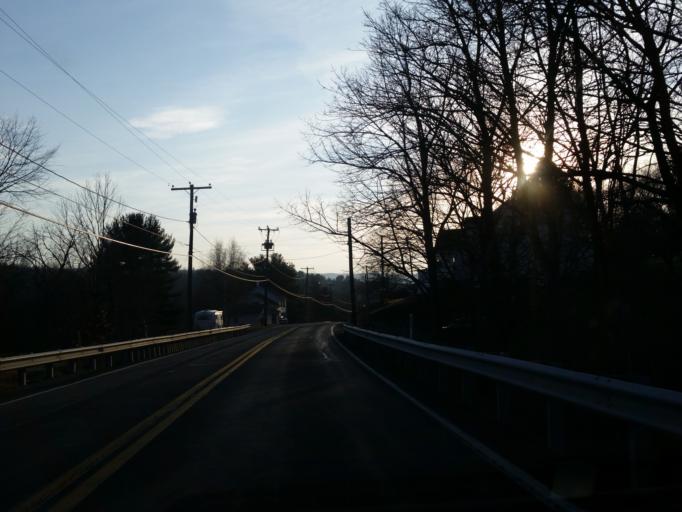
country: US
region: Pennsylvania
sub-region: Schuylkill County
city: Minersville
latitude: 40.6790
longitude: -76.2692
